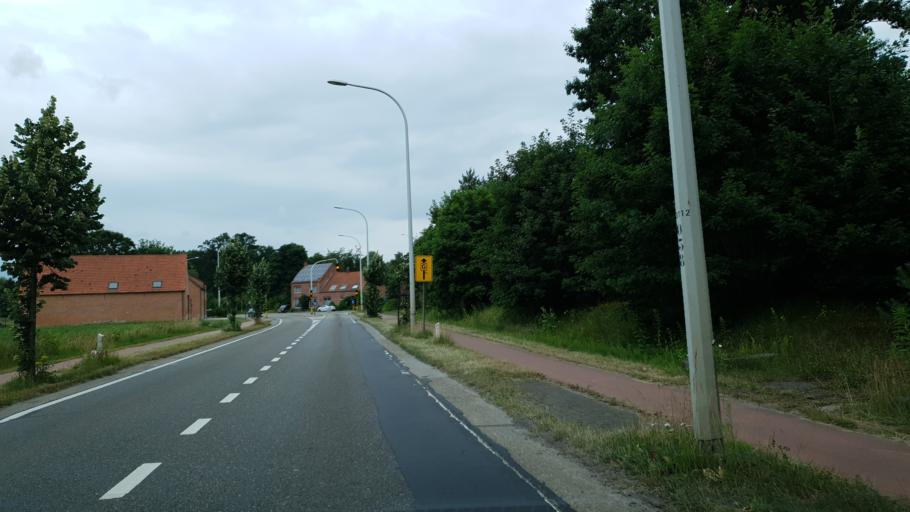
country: BE
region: Flanders
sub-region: Provincie Antwerpen
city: Geel
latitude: 51.1402
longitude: 5.0098
